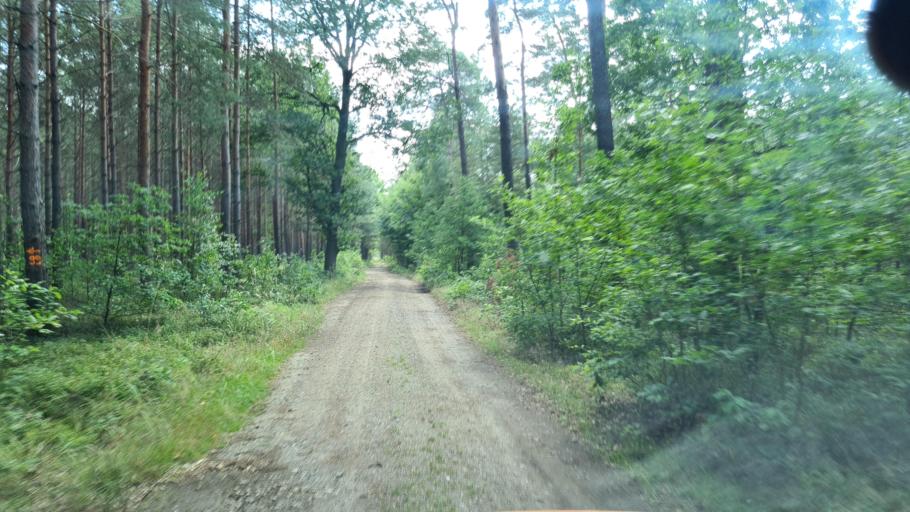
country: DE
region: Brandenburg
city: Hohenbucko
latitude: 51.7928
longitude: 13.5667
